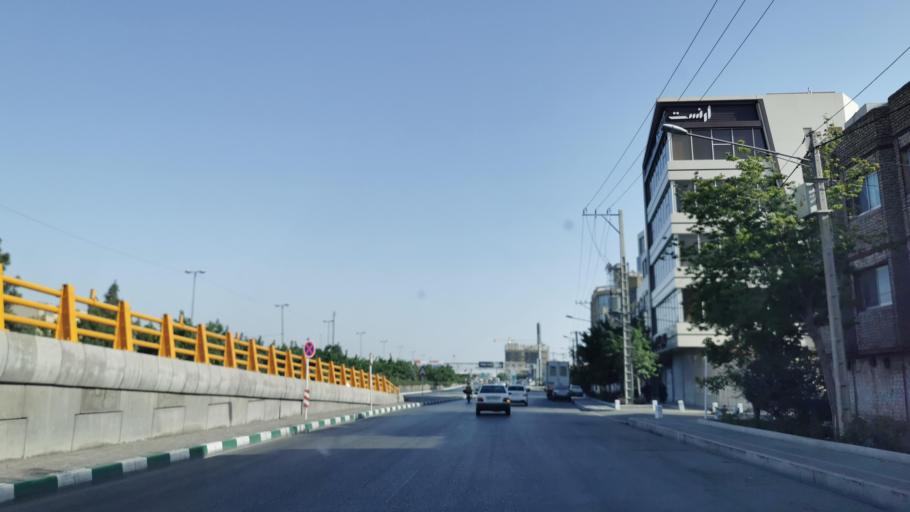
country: IR
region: Razavi Khorasan
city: Mashhad
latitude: 36.3638
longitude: 59.5381
